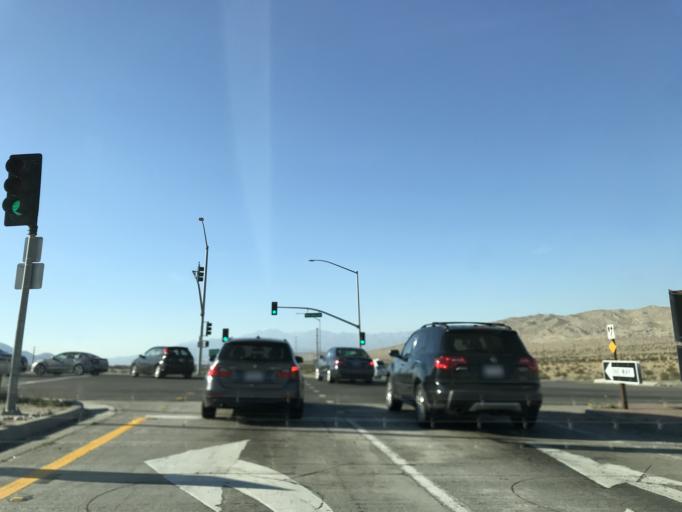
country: US
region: California
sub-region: Riverside County
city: Thousand Palms
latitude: 33.8208
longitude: -116.4080
